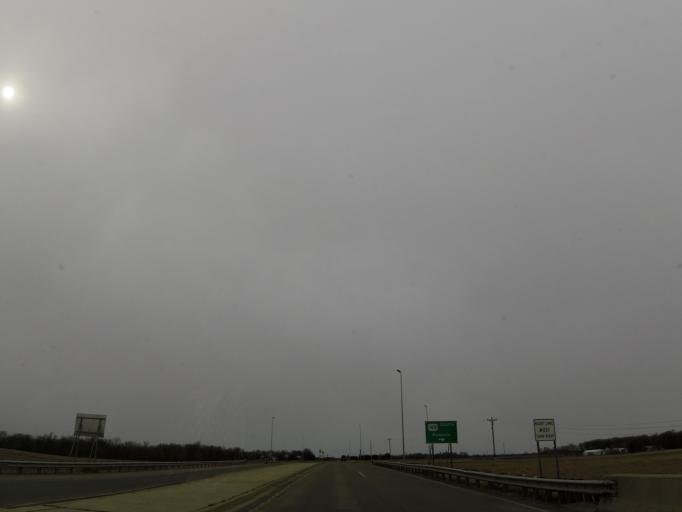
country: US
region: Minnesota
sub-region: Le Sueur County
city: Le Sueur
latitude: 44.5431
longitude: -93.8498
